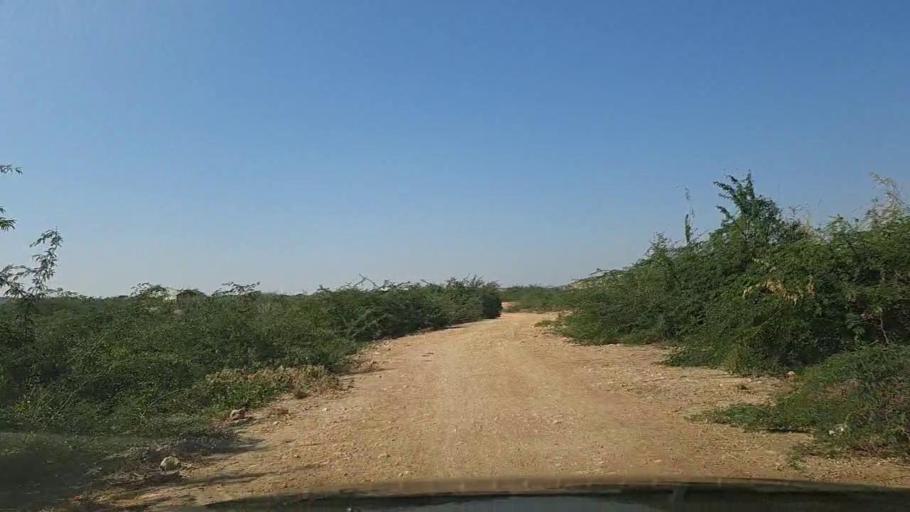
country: PK
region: Sindh
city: Thatta
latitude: 24.6298
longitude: 67.8671
